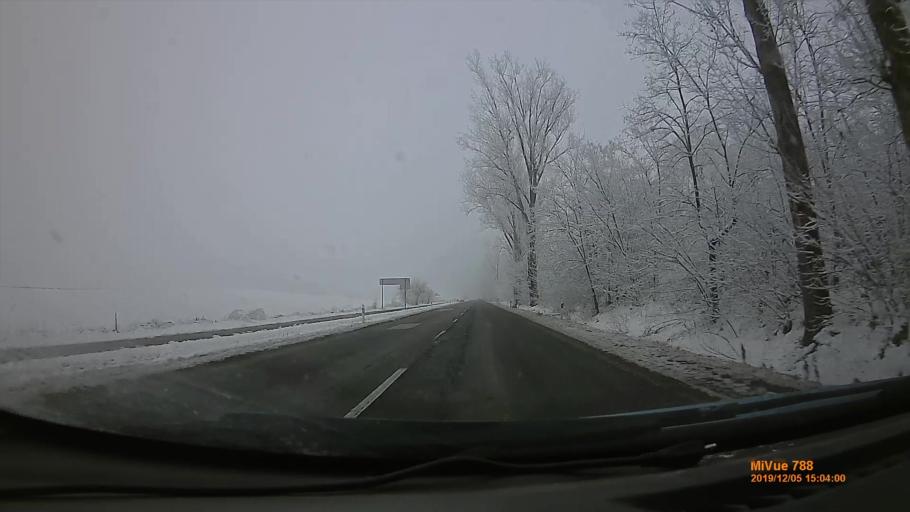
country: HU
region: Szabolcs-Szatmar-Bereg
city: Tiszanagyfalu
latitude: 48.0909
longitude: 21.4957
